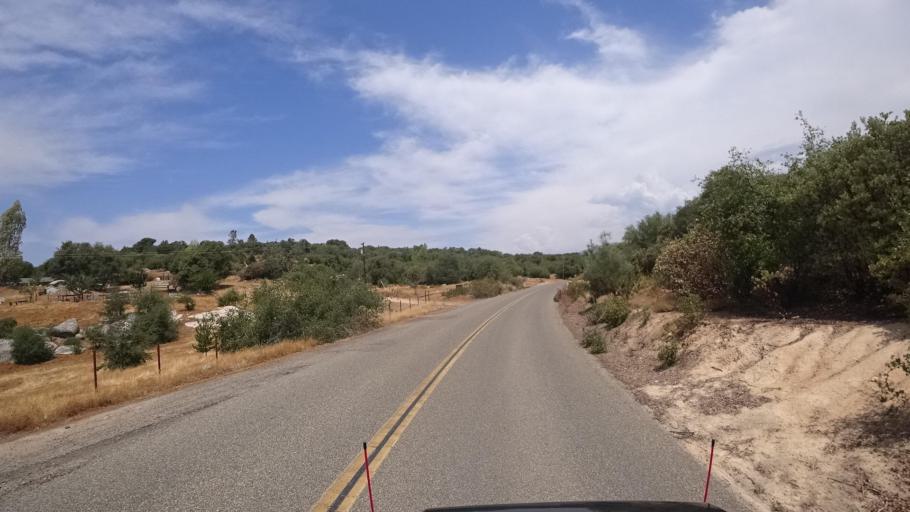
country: US
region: California
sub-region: Madera County
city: Ahwahnee
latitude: 37.4342
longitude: -119.8275
